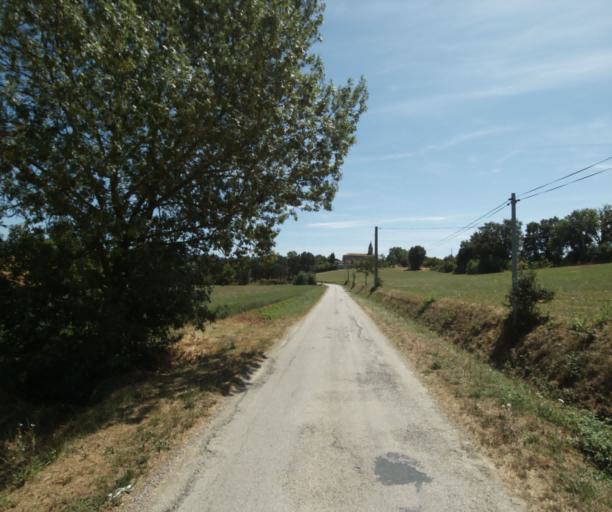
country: FR
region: Midi-Pyrenees
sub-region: Departement de la Haute-Garonne
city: Revel
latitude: 43.4943
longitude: 2.0176
